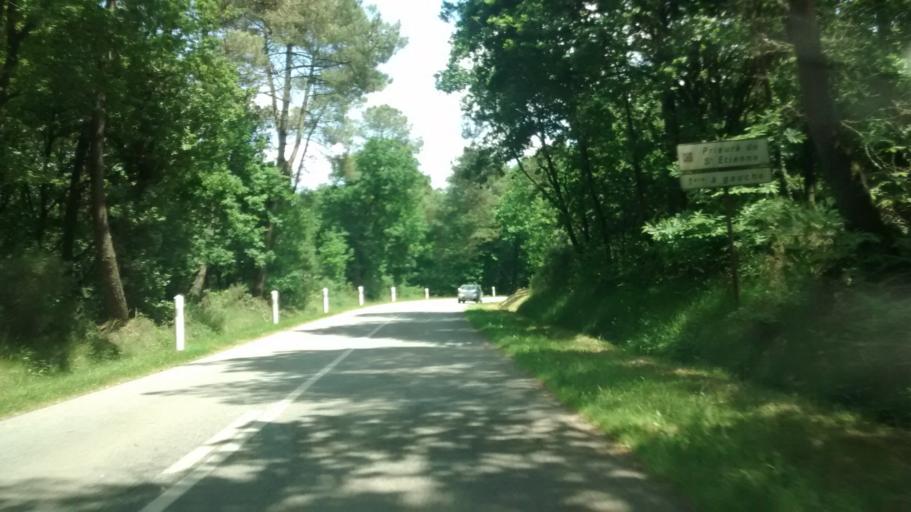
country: FR
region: Brittany
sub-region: Departement du Morbihan
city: Guer
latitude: 47.8904
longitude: -2.1628
